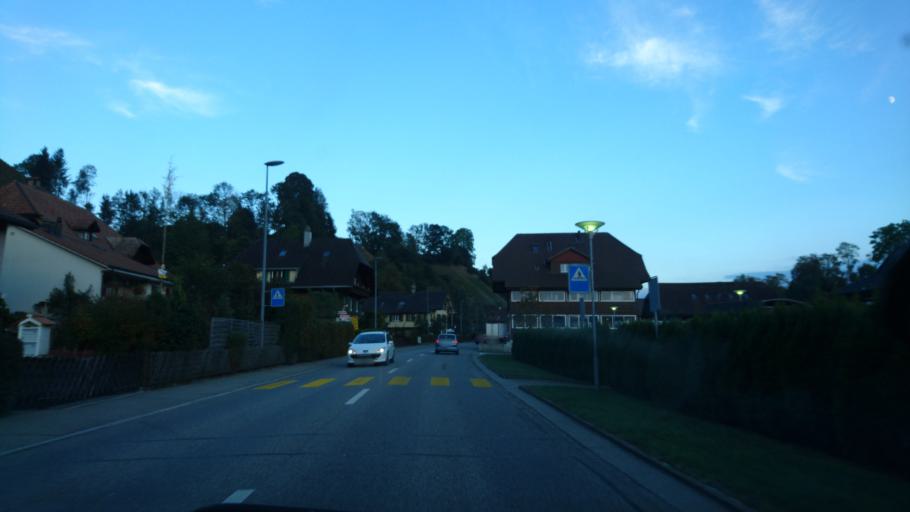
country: CH
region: Bern
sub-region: Emmental District
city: Langnau
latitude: 46.9383
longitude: 7.8006
